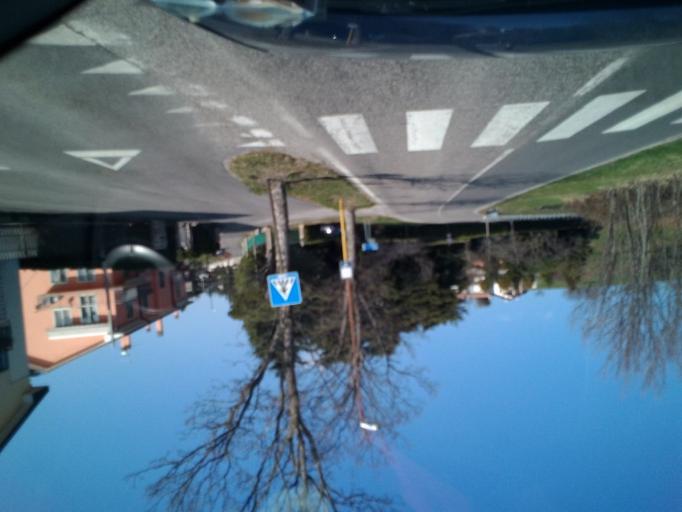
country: IT
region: Veneto
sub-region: Provincia di Verona
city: Cerro Veronese
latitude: 45.5845
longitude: 11.0387
